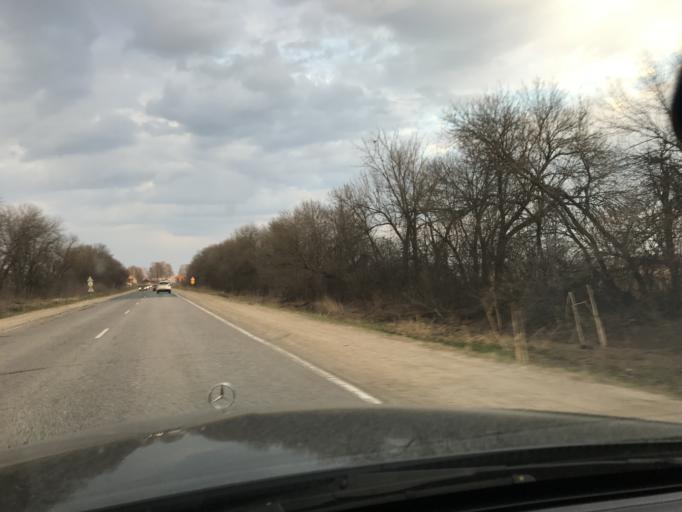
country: RU
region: Vladimir
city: Murom
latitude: 55.6176
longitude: 41.9348
